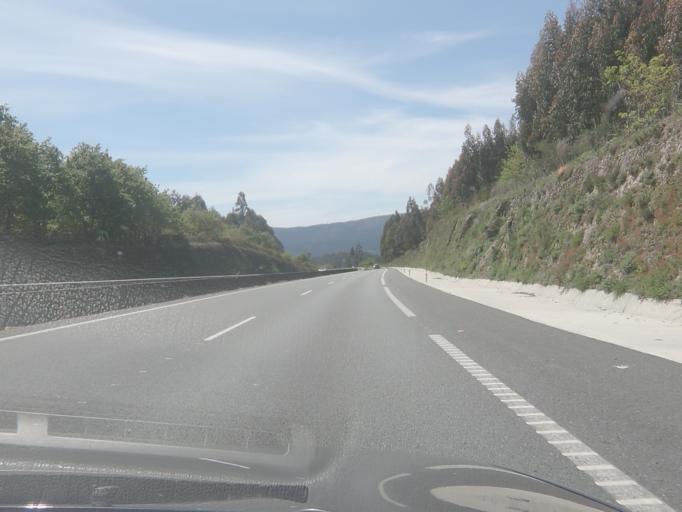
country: ES
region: Galicia
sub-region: Provincia da Coruna
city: Padron
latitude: 42.8069
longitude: -8.6086
